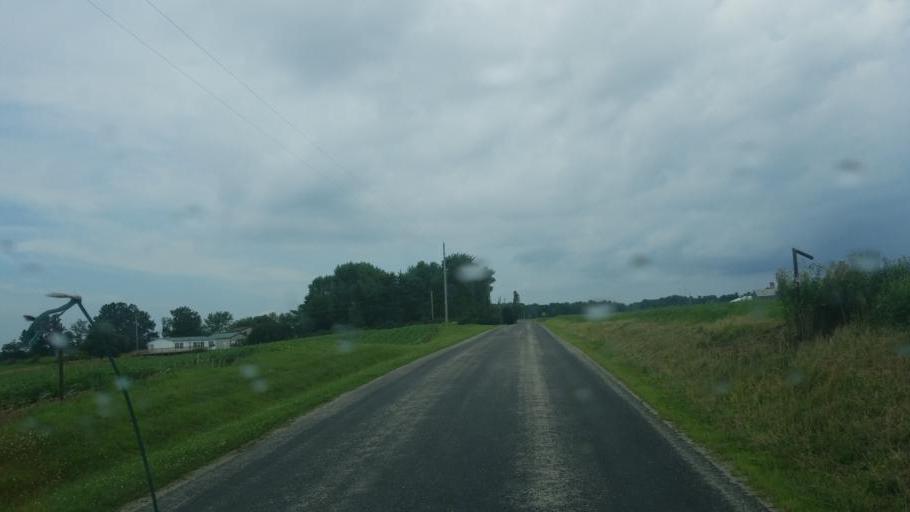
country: US
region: Ohio
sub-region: Wayne County
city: Wooster
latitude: 40.8840
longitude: -81.9933
